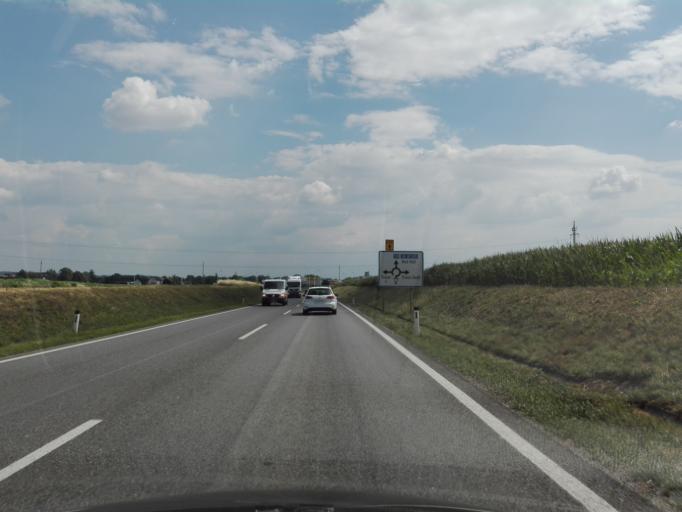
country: AT
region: Upper Austria
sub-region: Politischer Bezirk Linz-Land
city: Traun
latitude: 48.2263
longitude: 14.2235
